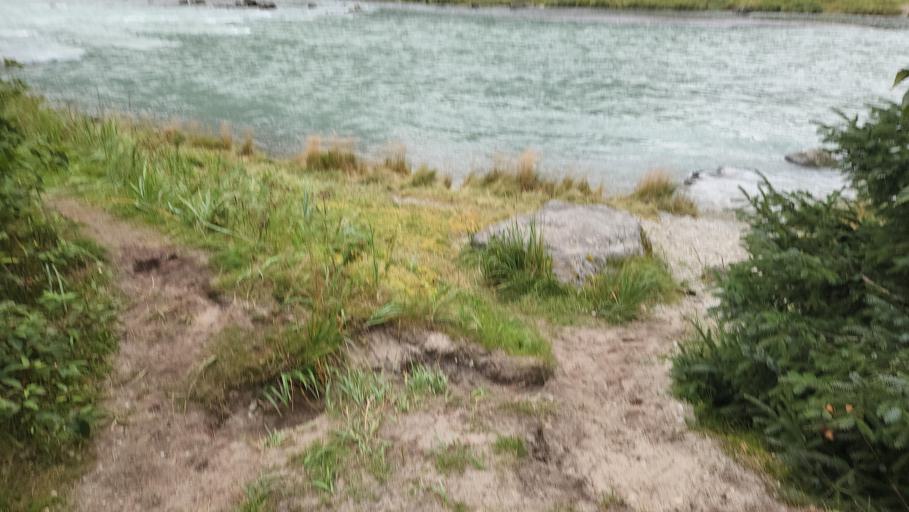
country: US
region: Alaska
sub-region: Haines Borough
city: Haines
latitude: 59.3239
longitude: -135.5566
